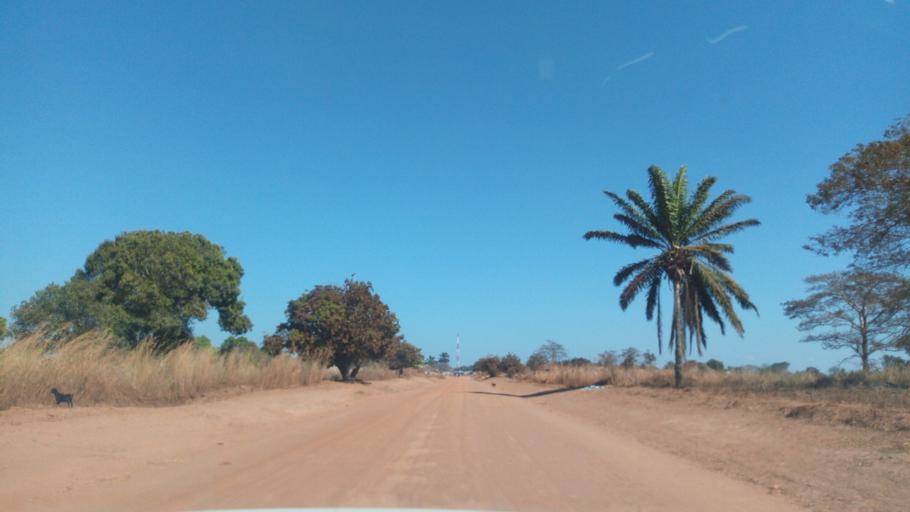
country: ZM
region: Luapula
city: Mwense
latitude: -10.7559
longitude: 28.2906
